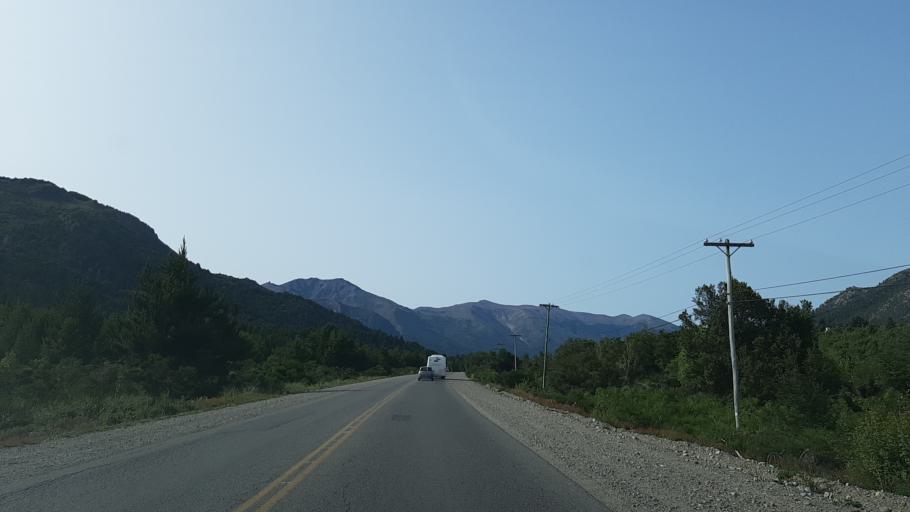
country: AR
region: Rio Negro
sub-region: Departamento de Bariloche
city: San Carlos de Bariloche
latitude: -41.1394
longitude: -71.4116
